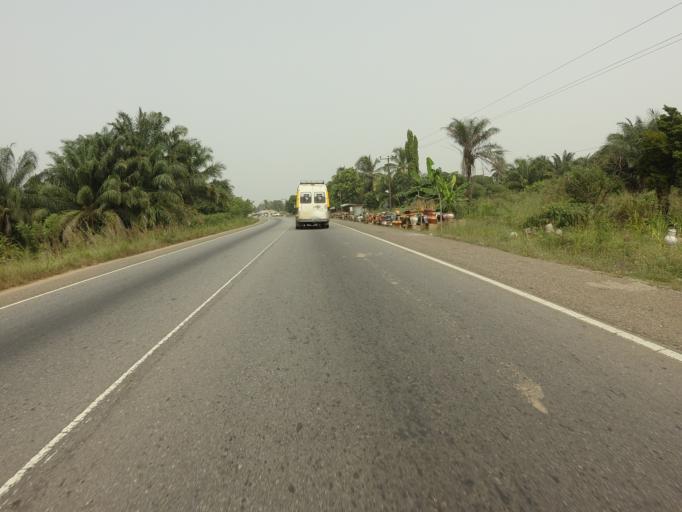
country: GH
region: Volta
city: Anloga
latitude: 6.0020
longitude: 0.5631
